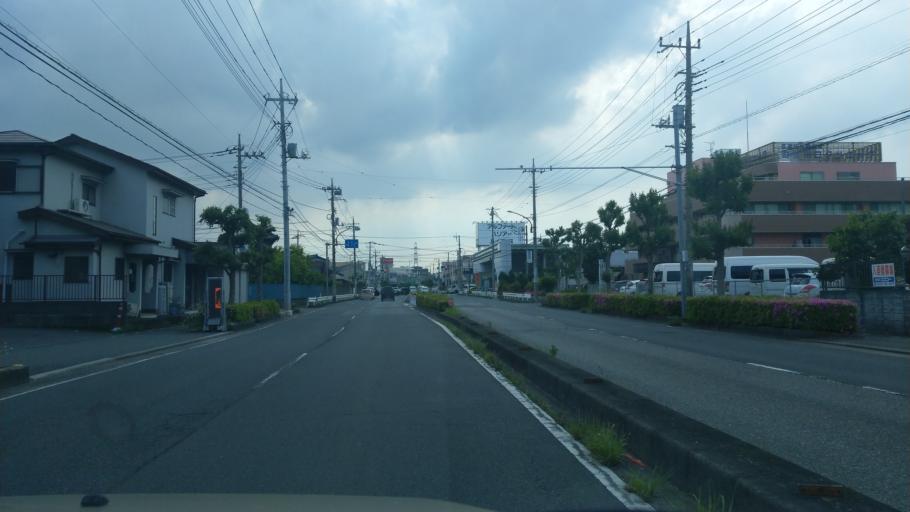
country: JP
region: Saitama
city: Koshigaya
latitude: 35.8664
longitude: 139.7551
